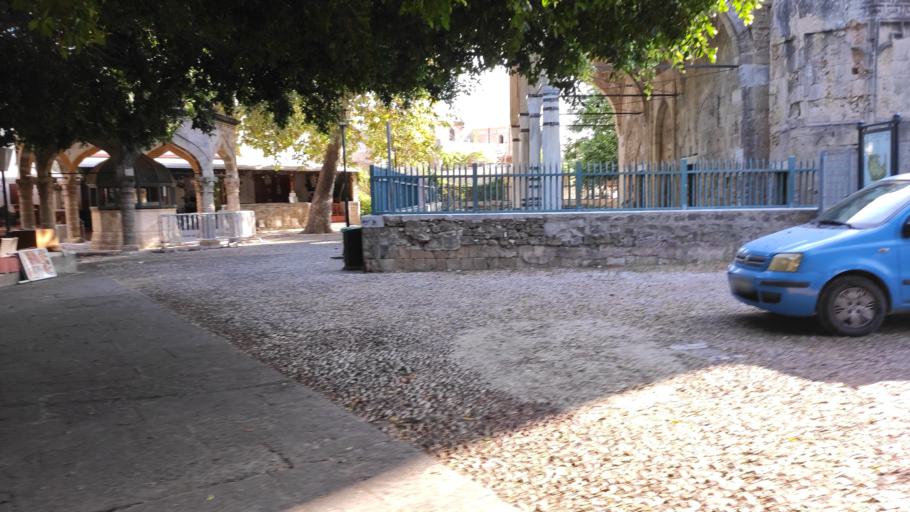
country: GR
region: South Aegean
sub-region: Nomos Dodekanisou
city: Rodos
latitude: 36.4415
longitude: 28.2263
